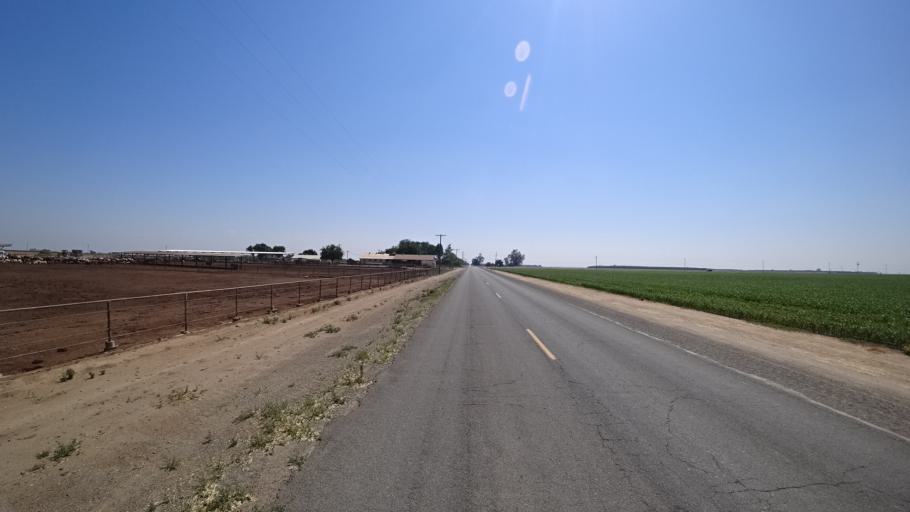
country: US
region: California
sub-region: Kings County
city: Hanford
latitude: 36.3720
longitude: -119.5685
